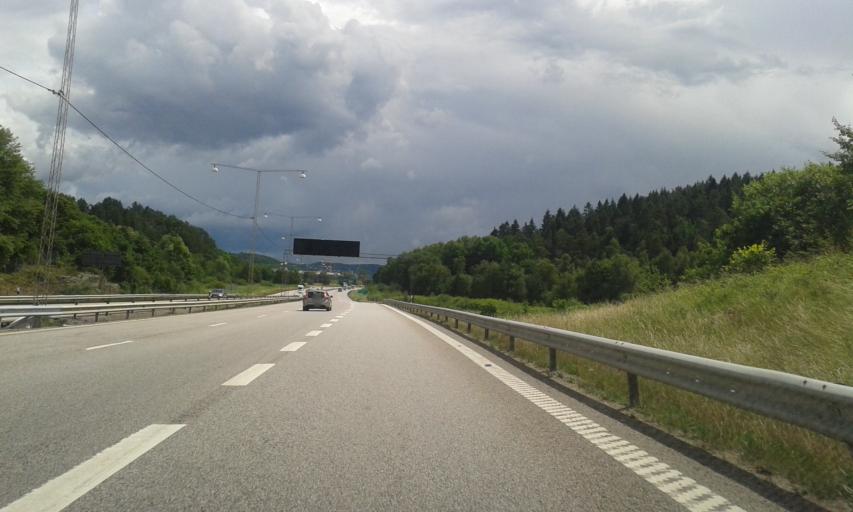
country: SE
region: Vaestra Goetaland
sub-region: Kungalvs Kommun
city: Kungalv
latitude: 57.8809
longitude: 11.9514
